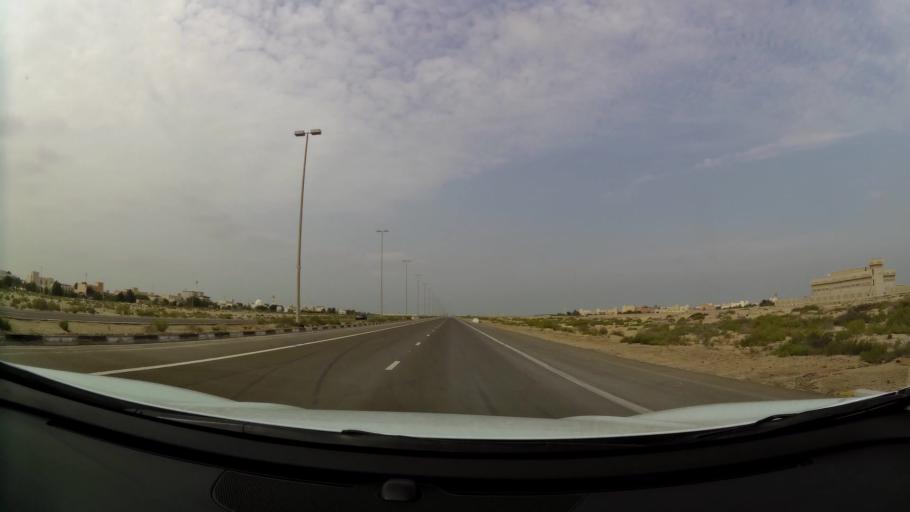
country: AE
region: Abu Dhabi
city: Abu Dhabi
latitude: 24.6376
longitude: 54.6761
